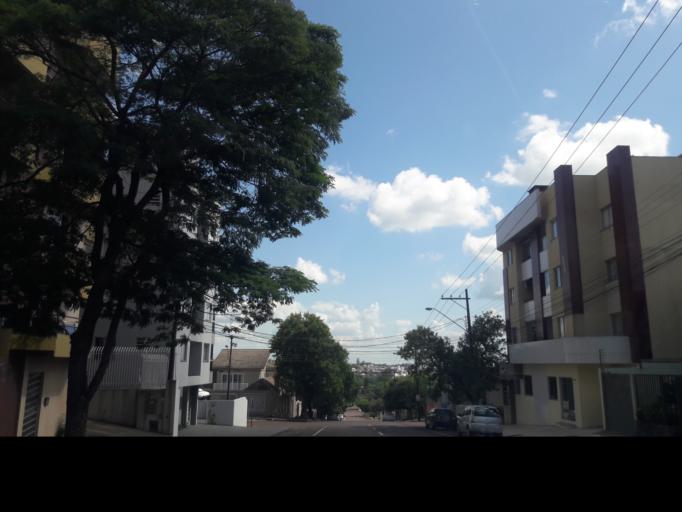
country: BR
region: Parana
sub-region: Cascavel
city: Cascavel
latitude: -24.9621
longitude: -53.4609
